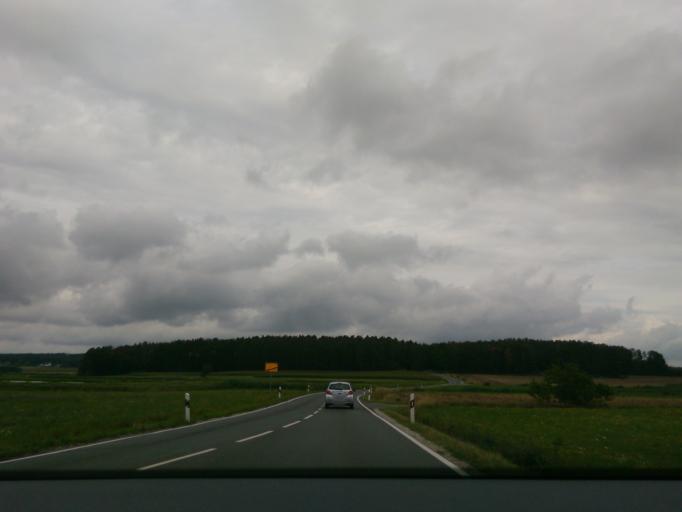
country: DE
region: Bavaria
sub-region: Regierungsbezirk Mittelfranken
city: Weisendorf
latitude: 49.6361
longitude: 10.8191
